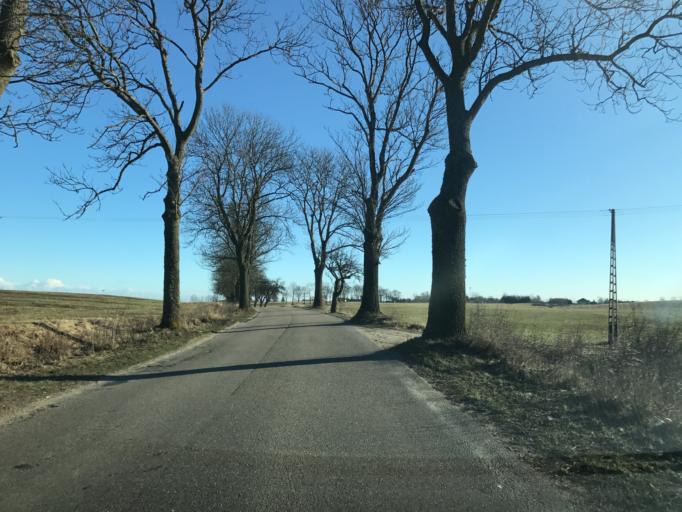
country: PL
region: Warmian-Masurian Voivodeship
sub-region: Powiat olsztynski
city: Jonkowo
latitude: 53.9241
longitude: 20.2259
